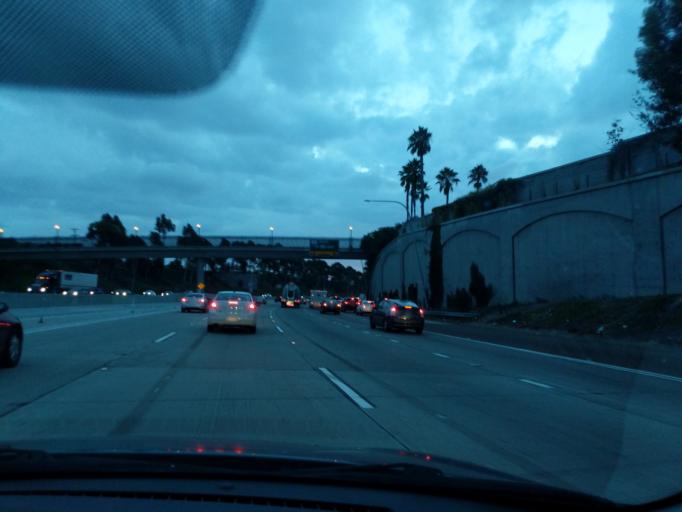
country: US
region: California
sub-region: San Diego County
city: San Diego
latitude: 32.7466
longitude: -117.1091
